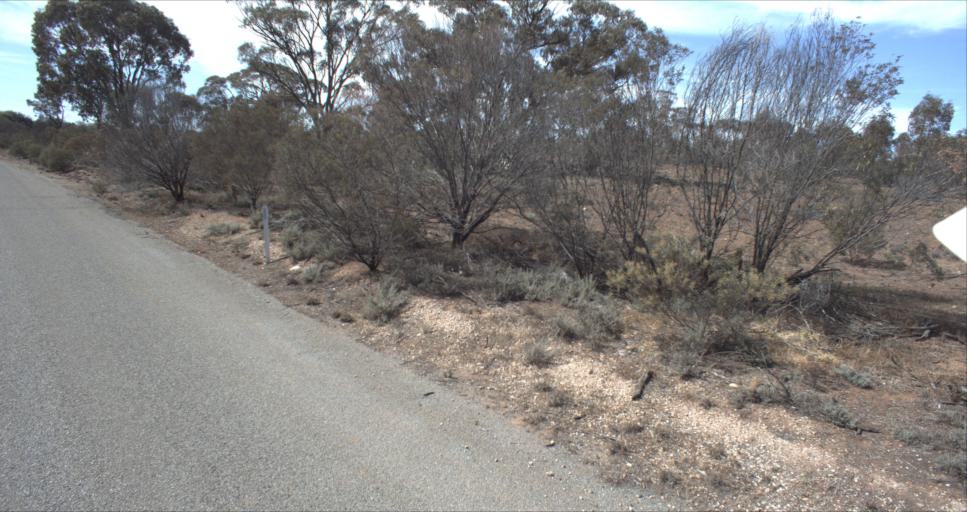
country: AU
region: New South Wales
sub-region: Leeton
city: Leeton
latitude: -34.5827
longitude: 146.4590
